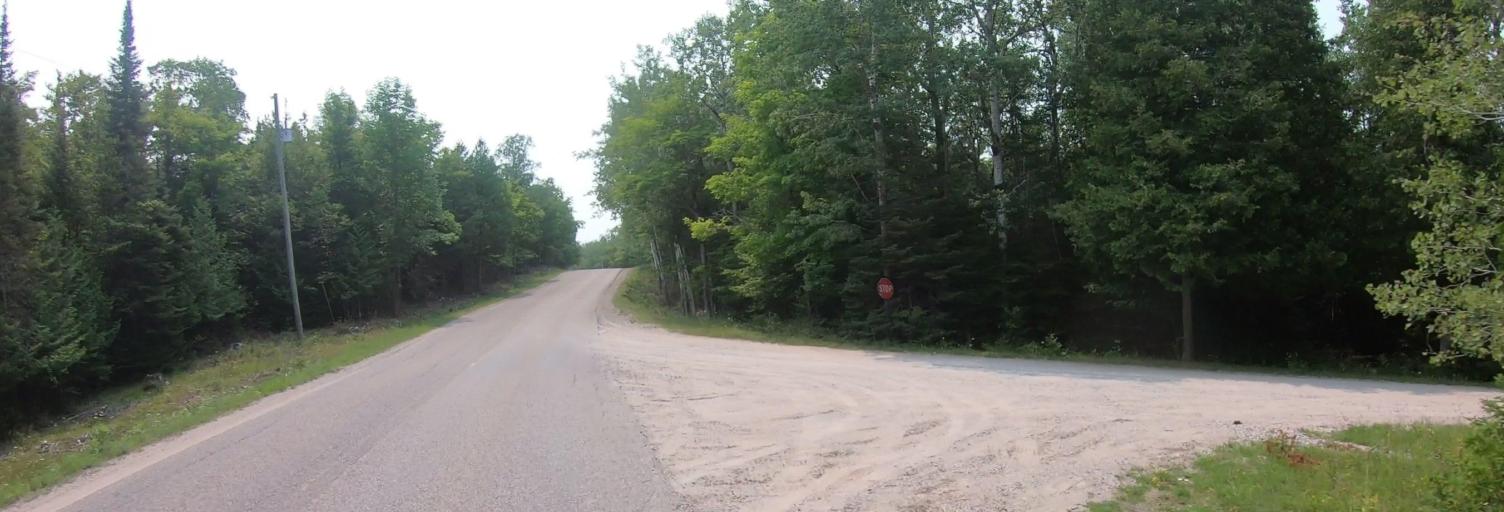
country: CA
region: Ontario
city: Thessalon
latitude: 46.0281
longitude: -83.6775
